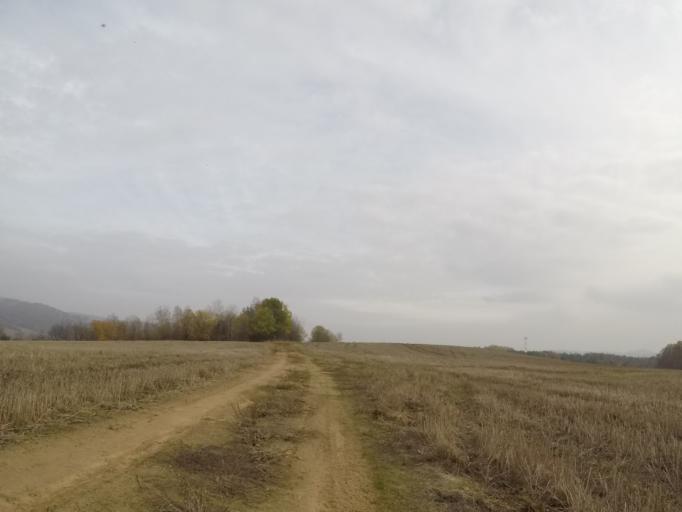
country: SK
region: Presovsky
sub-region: Okres Presov
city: Presov
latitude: 48.9384
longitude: 21.1620
